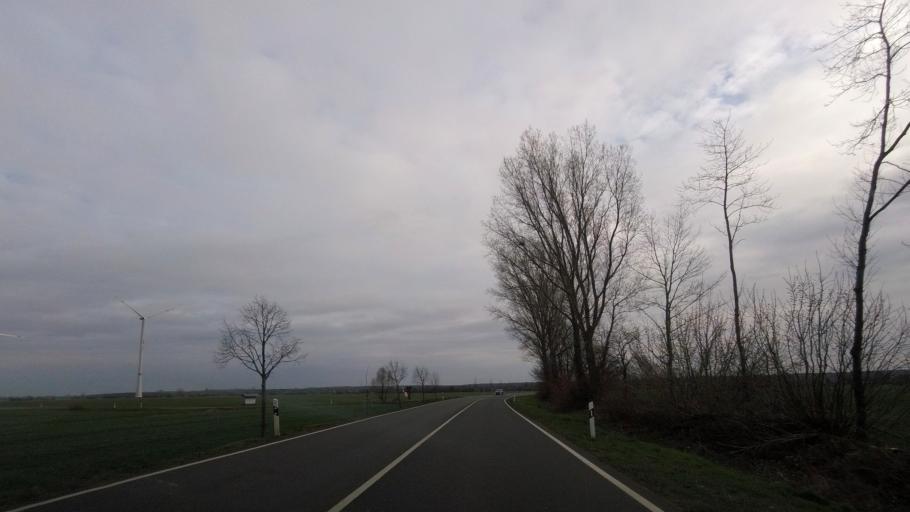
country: DE
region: Saxony-Anhalt
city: Kemberg
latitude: 51.7833
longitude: 12.6480
